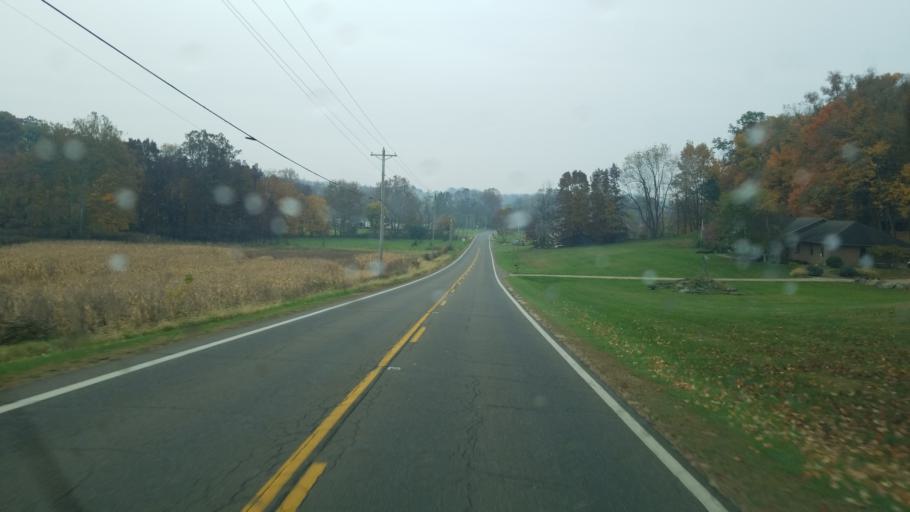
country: US
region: Ohio
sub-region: Holmes County
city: Millersburg
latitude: 40.4581
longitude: -81.9008
